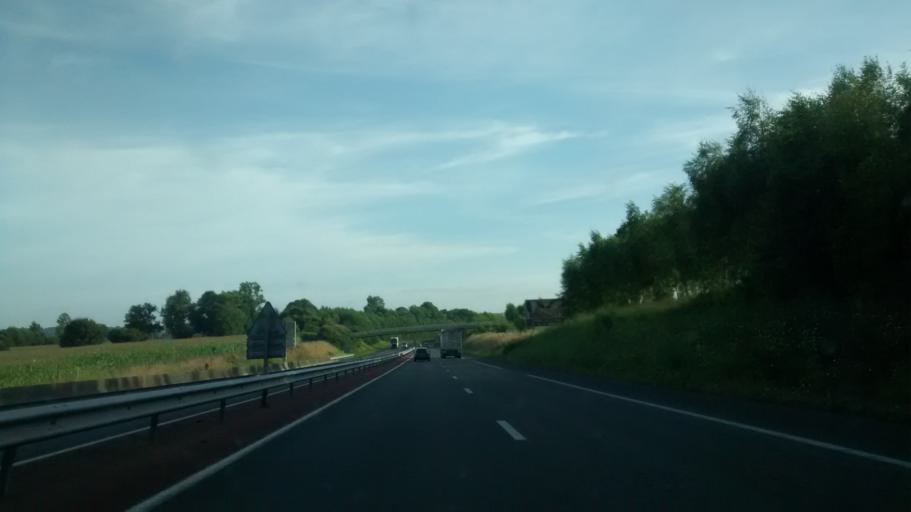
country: FR
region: Lower Normandy
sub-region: Departement de la Manche
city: Saint-Senier-sous-Avranches
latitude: 48.7341
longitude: -1.2958
